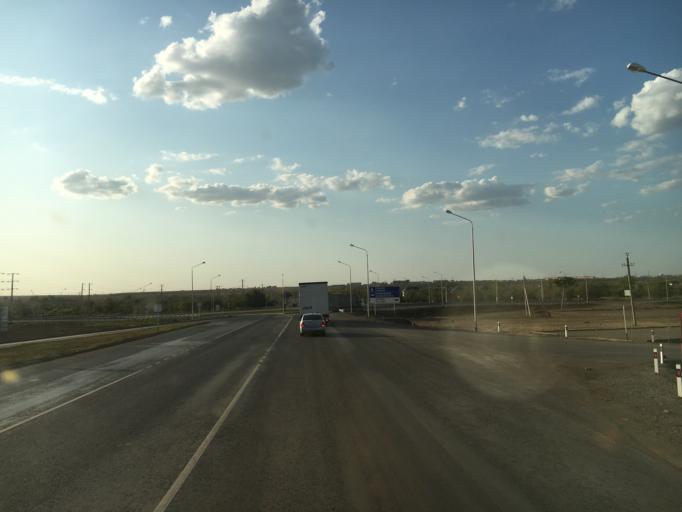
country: KZ
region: Aqtoebe
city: Aqtobe
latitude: 50.2388
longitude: 57.1646
